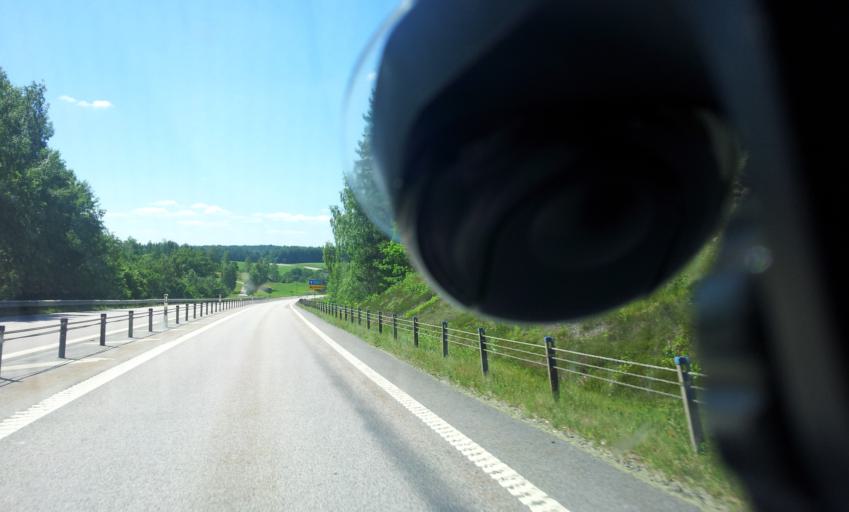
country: SE
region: Kalmar
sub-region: Vasterviks Kommun
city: Forserum
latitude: 58.0122
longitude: 16.5081
